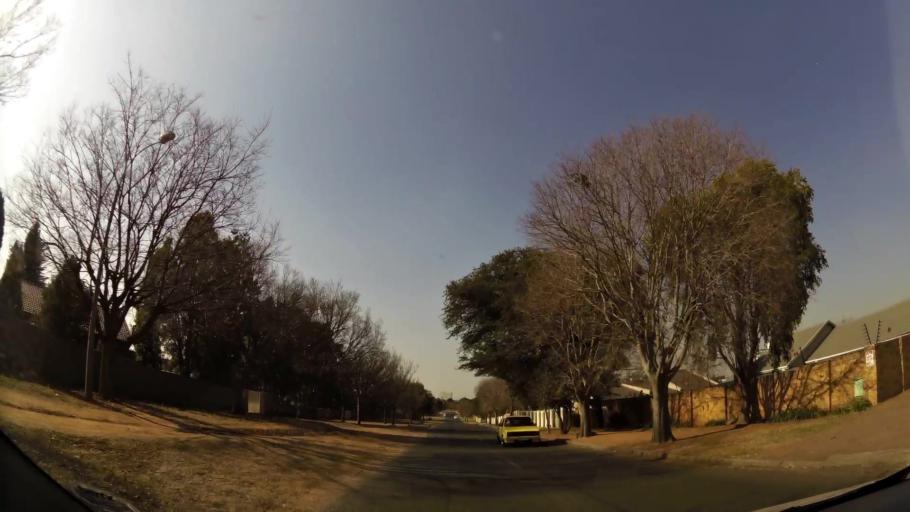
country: ZA
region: Gauteng
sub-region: West Rand District Municipality
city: Randfontein
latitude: -26.1856
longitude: 27.6824
